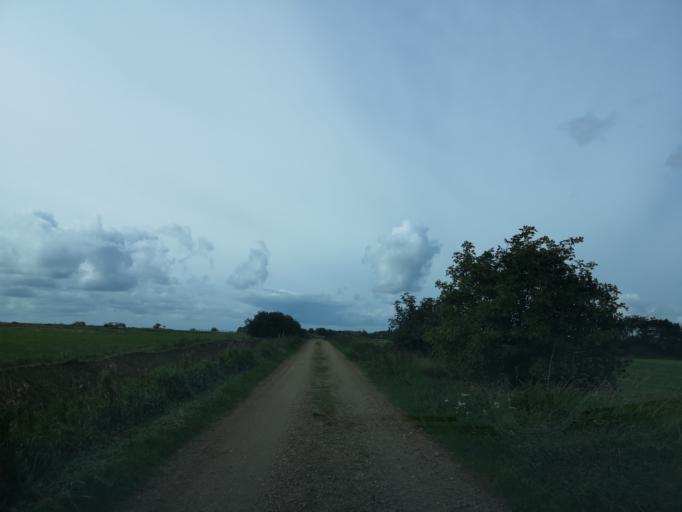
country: DK
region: Central Jutland
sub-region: Ringkobing-Skjern Kommune
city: Tarm
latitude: 55.9310
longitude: 8.5185
